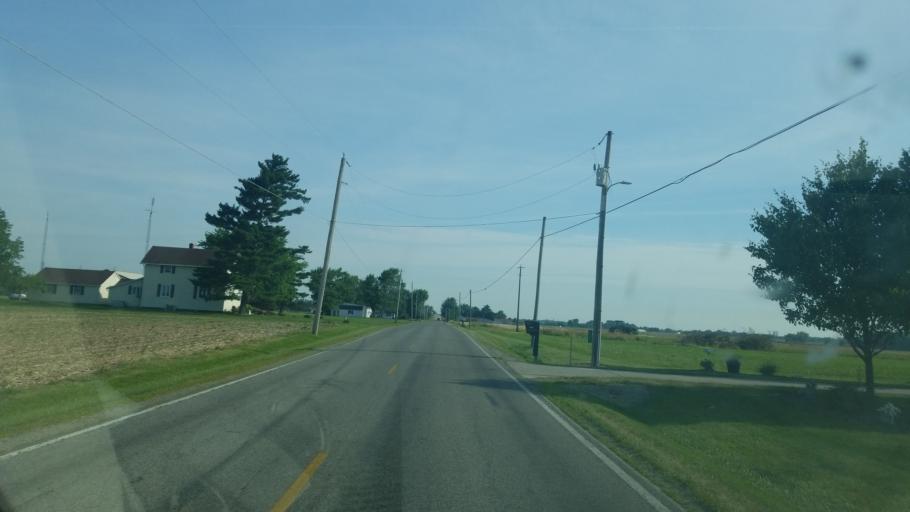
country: US
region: Ohio
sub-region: Hancock County
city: Findlay
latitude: 40.9847
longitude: -83.6985
